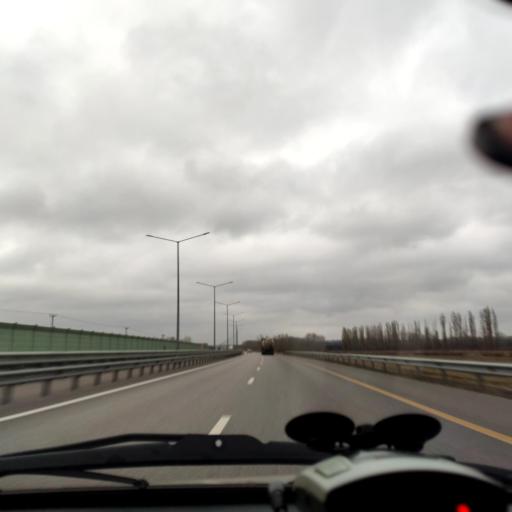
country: RU
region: Voronezj
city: Novaya Usman'
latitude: 51.5899
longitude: 39.3799
